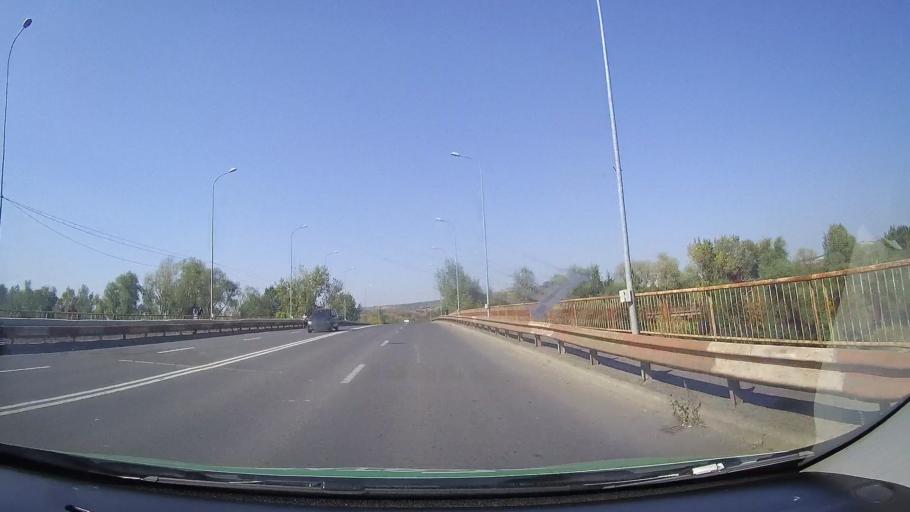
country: RO
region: Arad
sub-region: Oras Lipova
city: Radna
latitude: 46.0910
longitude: 21.6886
